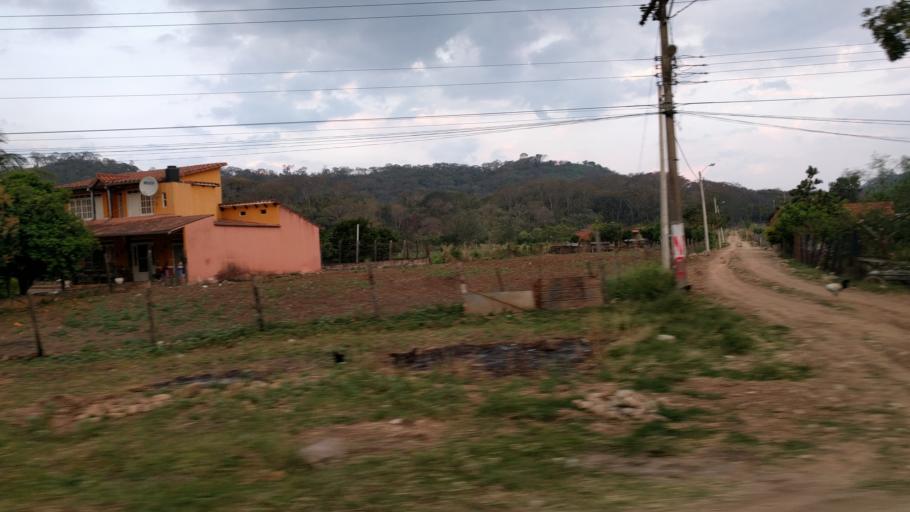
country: BO
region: Santa Cruz
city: Jorochito
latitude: -18.0958
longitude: -63.4506
